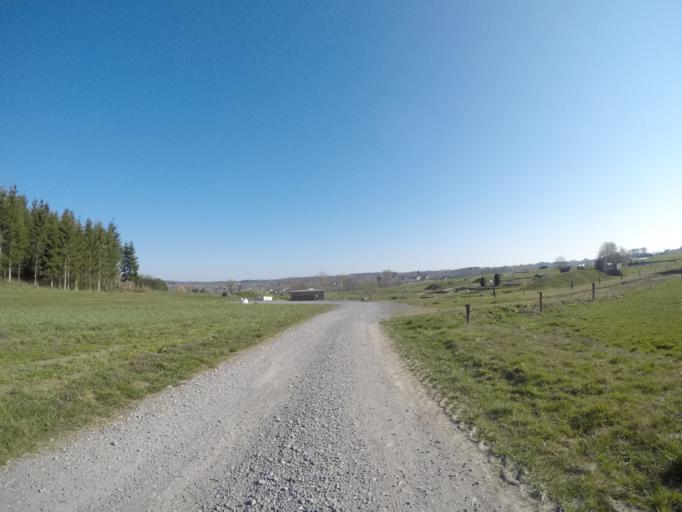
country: BE
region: Wallonia
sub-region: Province du Luxembourg
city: Habay-la-Vieille
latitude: 49.7153
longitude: 5.6142
